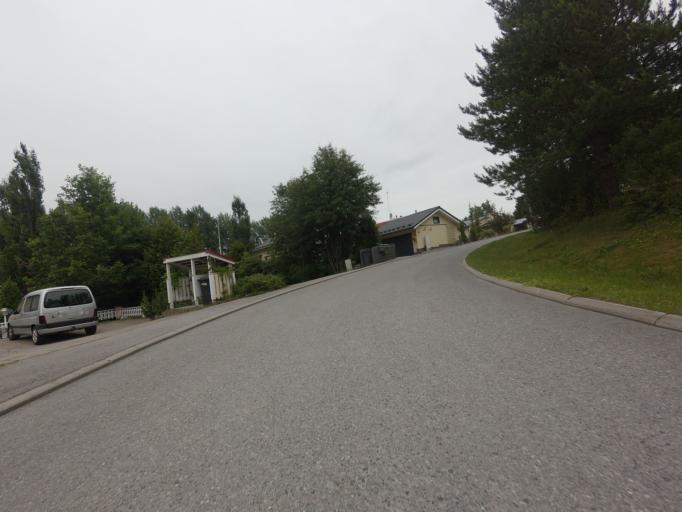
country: FI
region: Uusimaa
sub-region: Helsinki
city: Kauniainen
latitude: 60.1914
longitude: 24.7296
